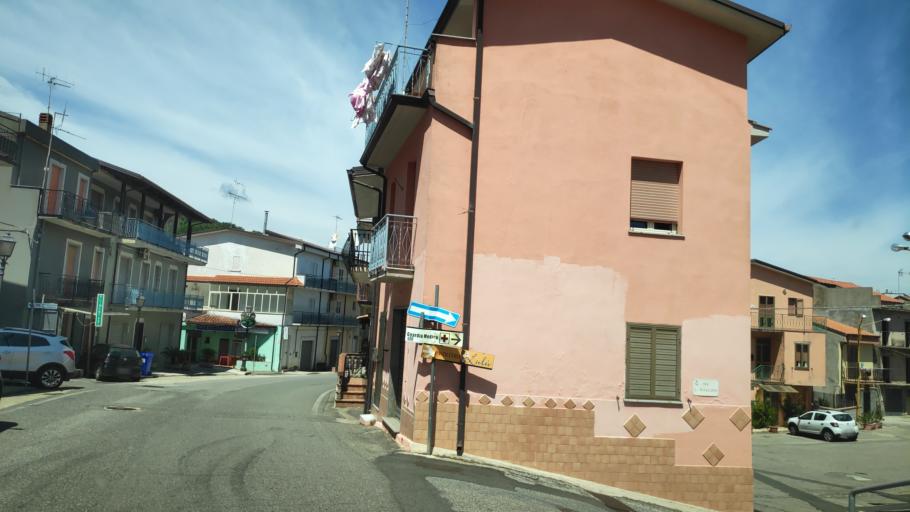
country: IT
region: Calabria
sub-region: Provincia di Catanzaro
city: Palermiti
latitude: 38.7496
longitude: 16.4533
